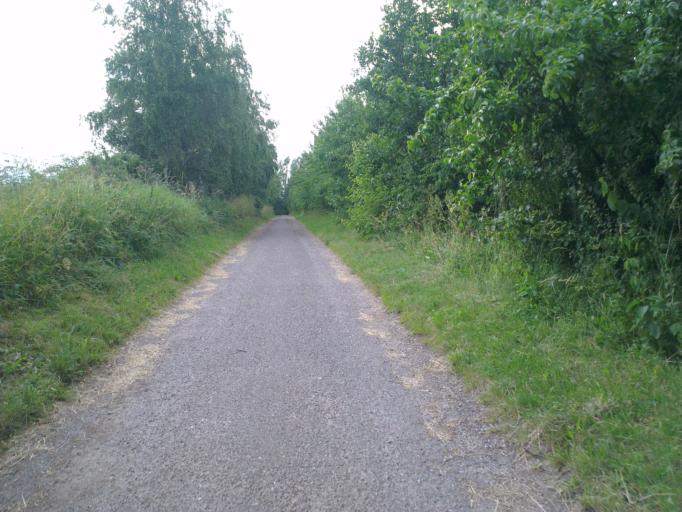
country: DK
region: Capital Region
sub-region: Frederikssund Kommune
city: Skibby
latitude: 55.7420
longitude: 11.9836
